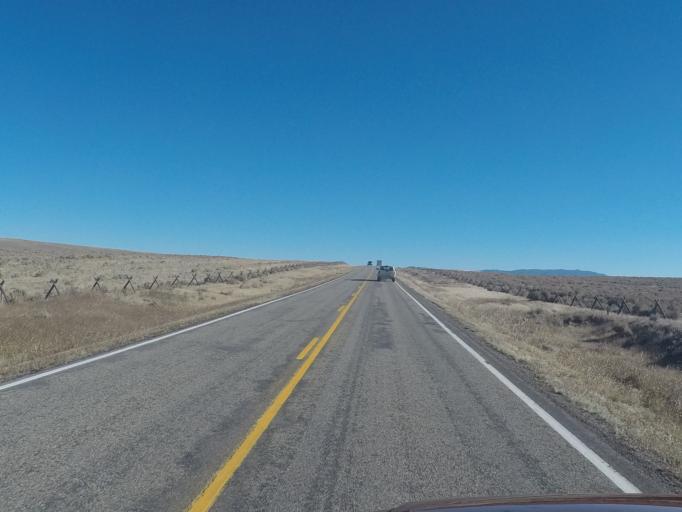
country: US
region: Montana
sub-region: Meagher County
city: White Sulphur Springs
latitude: 46.3661
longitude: -111.0075
